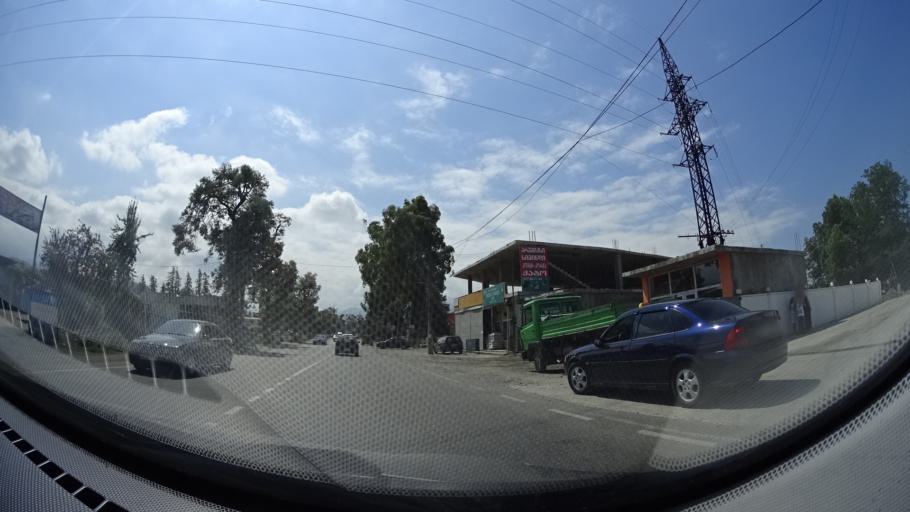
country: GE
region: Ajaria
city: Batumi
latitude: 41.6195
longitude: 41.6174
